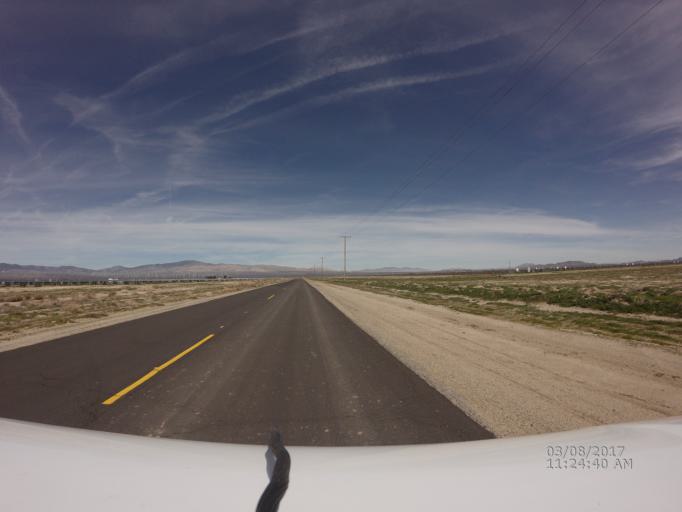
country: US
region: California
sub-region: Los Angeles County
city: Green Valley
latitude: 34.8124
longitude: -118.3791
